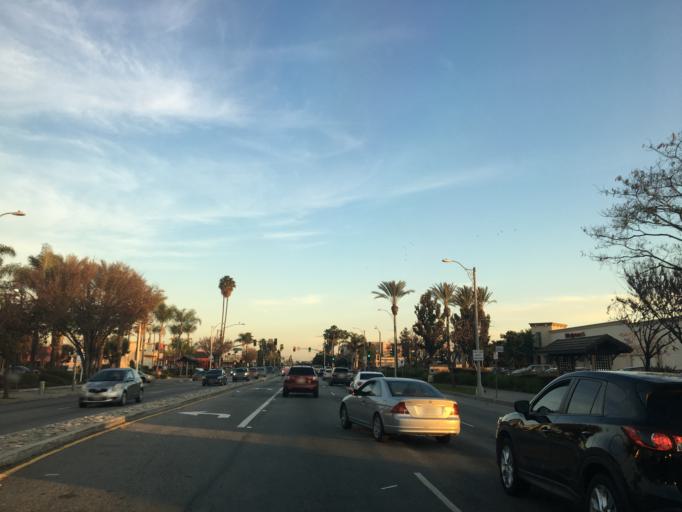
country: US
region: California
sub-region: Los Angeles County
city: Pico Rivera
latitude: 33.9839
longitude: -118.0984
